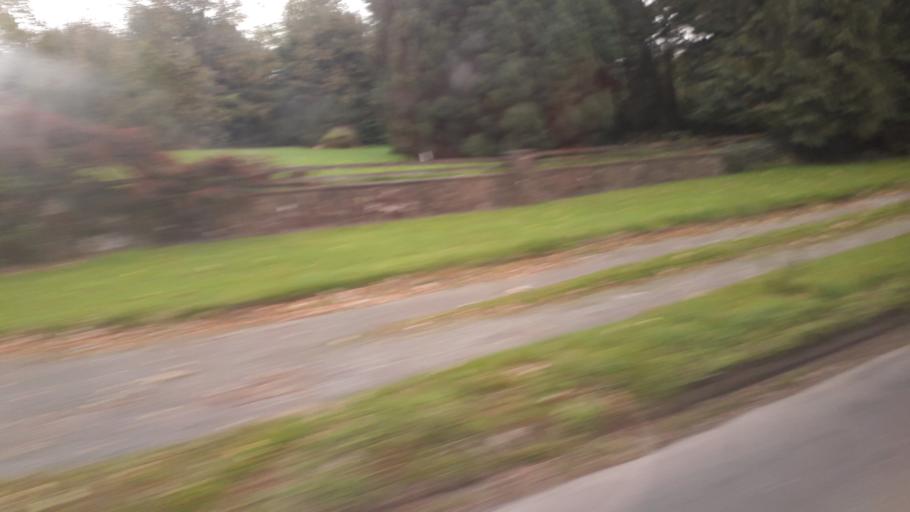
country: IE
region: Munster
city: Ballina
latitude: 52.7942
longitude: -8.4349
